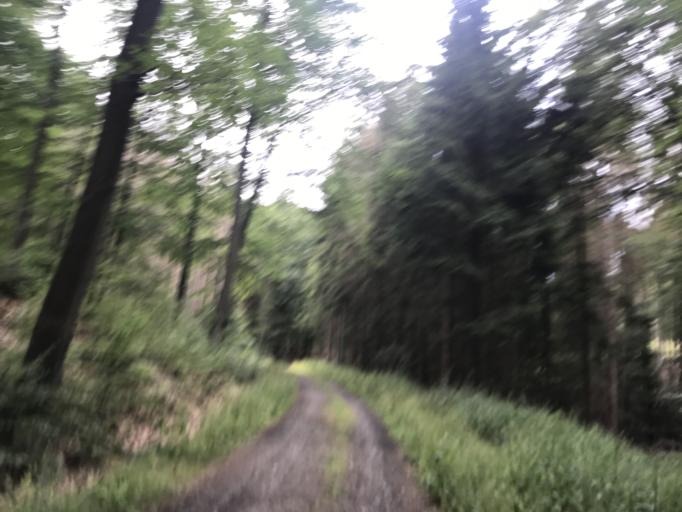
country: DE
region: Hesse
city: Lollar
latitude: 50.6513
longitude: 8.6384
